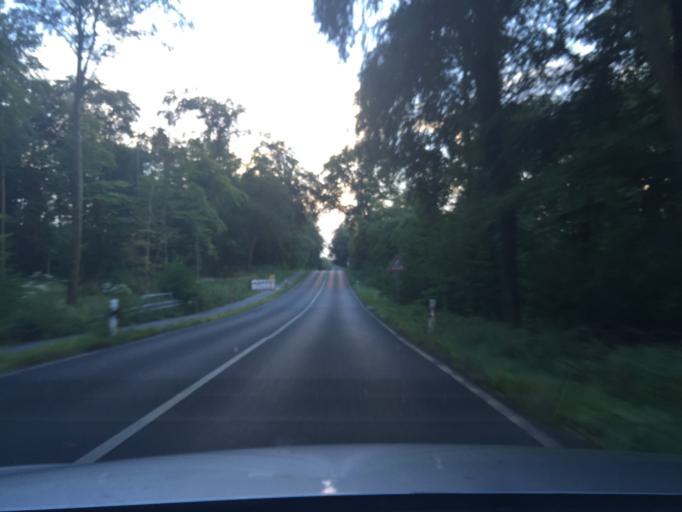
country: DE
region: North Rhine-Westphalia
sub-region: Regierungsbezirk Dusseldorf
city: Ratingen
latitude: 51.3422
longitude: 6.8771
